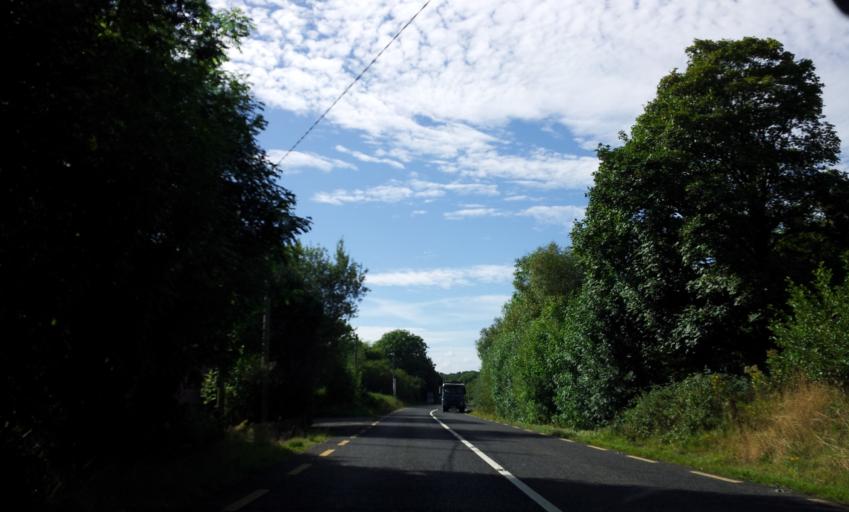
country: IE
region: Munster
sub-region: County Cork
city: Macroom
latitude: 51.9065
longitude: -9.0063
